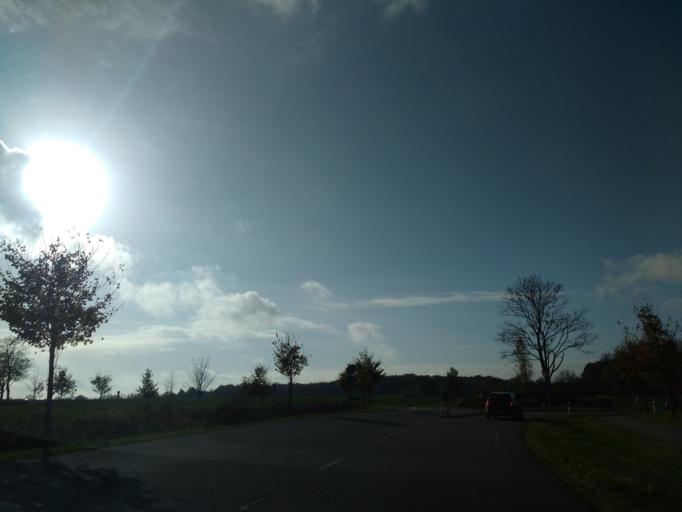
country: DE
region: Mecklenburg-Vorpommern
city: Ostseebad Boltenhagen
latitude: 53.9561
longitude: 11.2239
